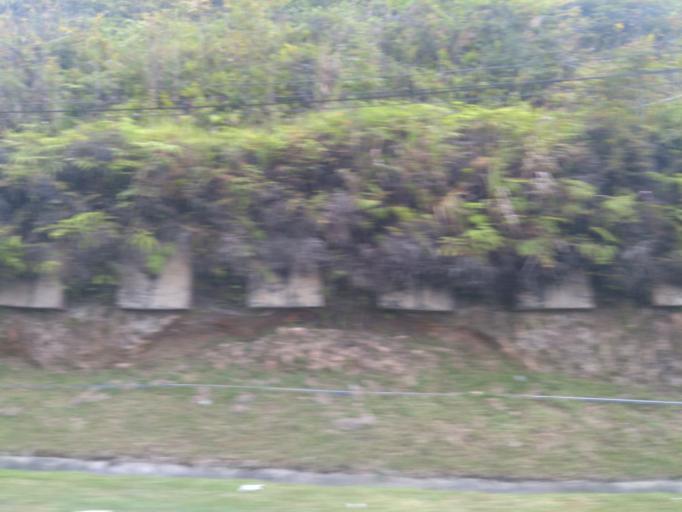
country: MY
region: Pahang
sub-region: Cameron Highlands
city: Tanah Rata
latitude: 4.5734
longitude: 101.4162
